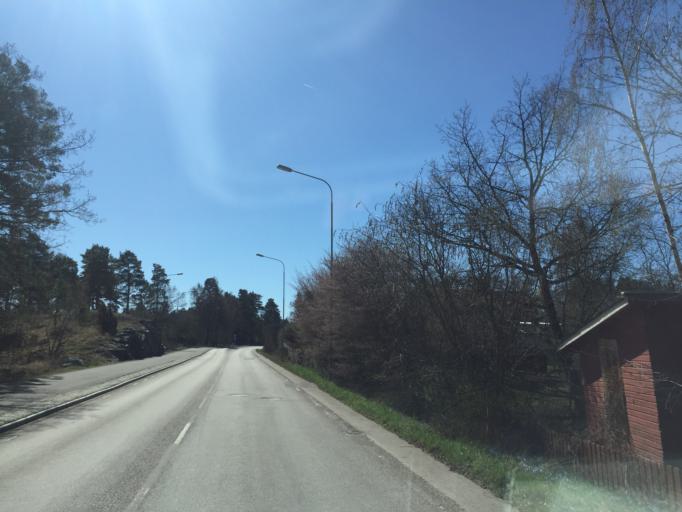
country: SE
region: Kalmar
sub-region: Oskarshamns Kommun
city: Oskarshamn
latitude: 57.2516
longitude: 16.4607
